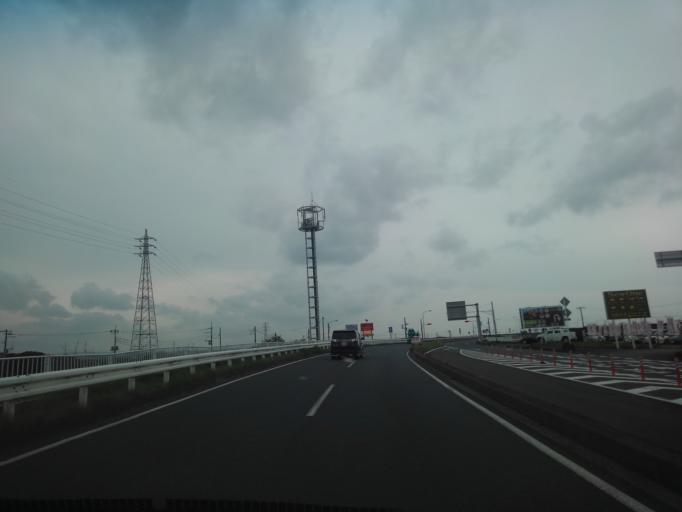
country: JP
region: Chiba
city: Kisarazu
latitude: 35.4122
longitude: 139.9555
